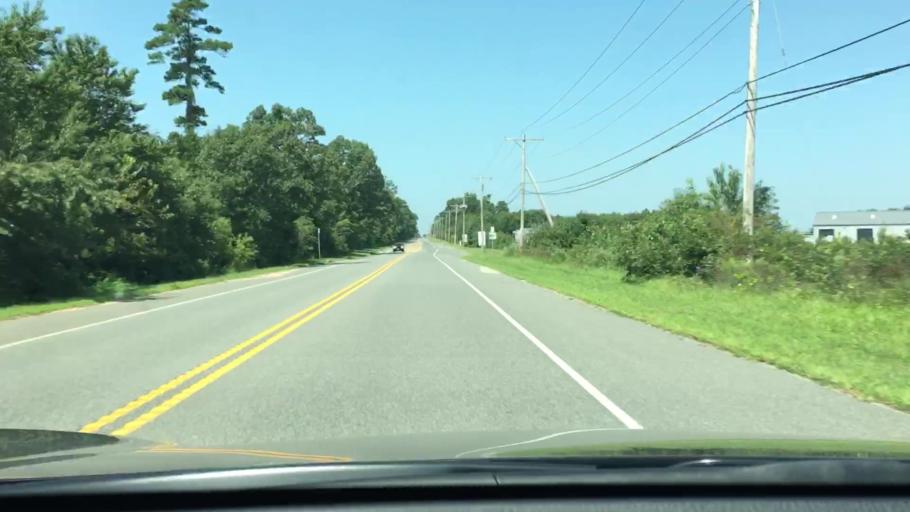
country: US
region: New Jersey
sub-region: Cumberland County
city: Laurel Lake
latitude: 39.3542
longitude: -75.0616
